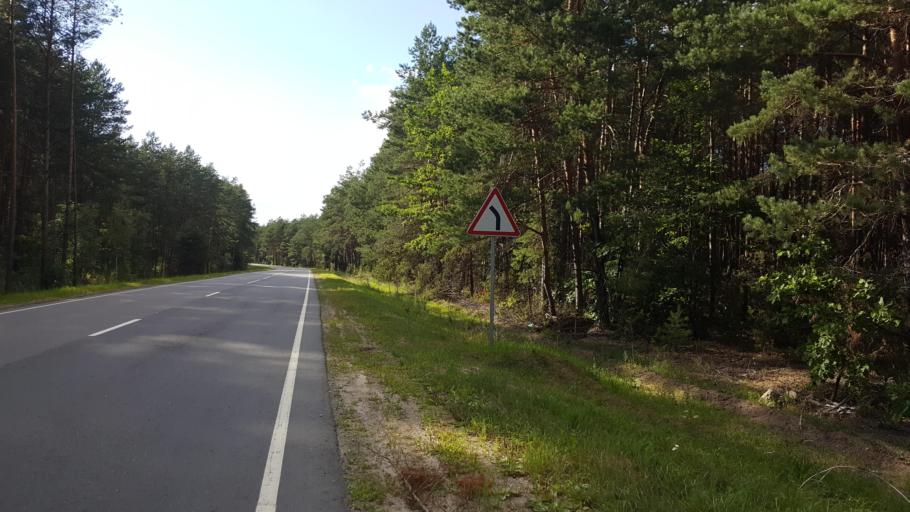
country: BY
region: Brest
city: Zhabinka
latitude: 52.3977
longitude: 24.0884
